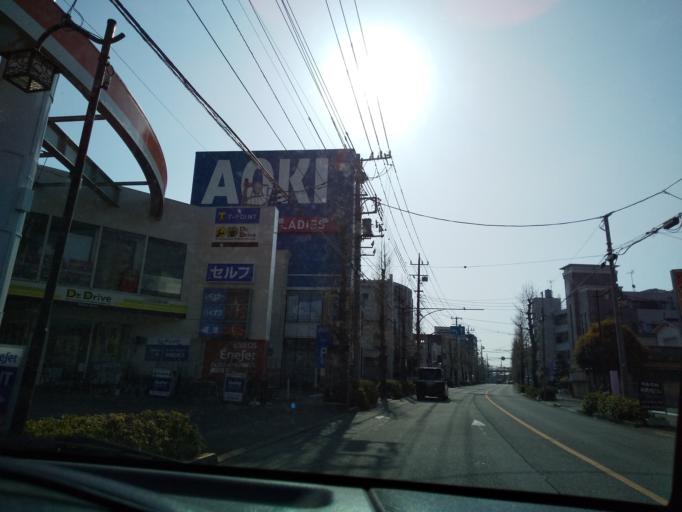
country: JP
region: Tokyo
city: Hino
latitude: 35.7102
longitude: 139.3674
